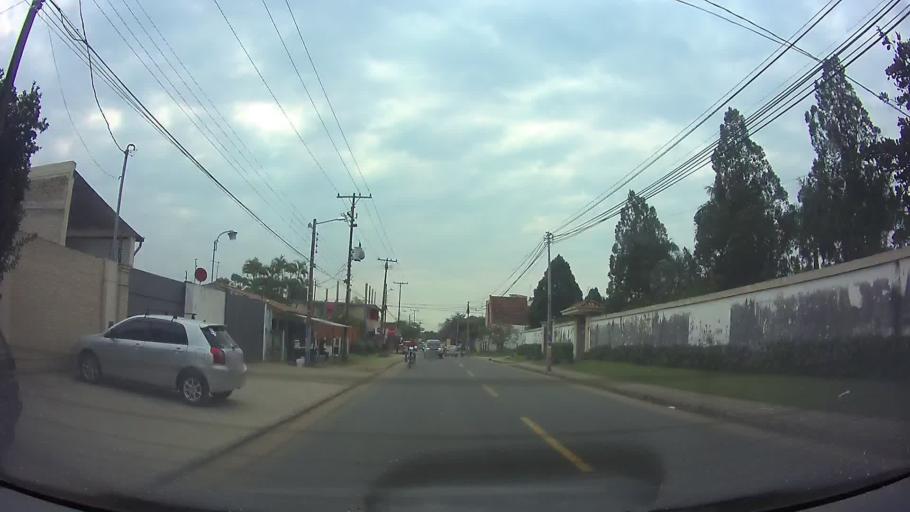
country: PY
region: Central
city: Fernando de la Mora
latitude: -25.2864
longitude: -57.5375
